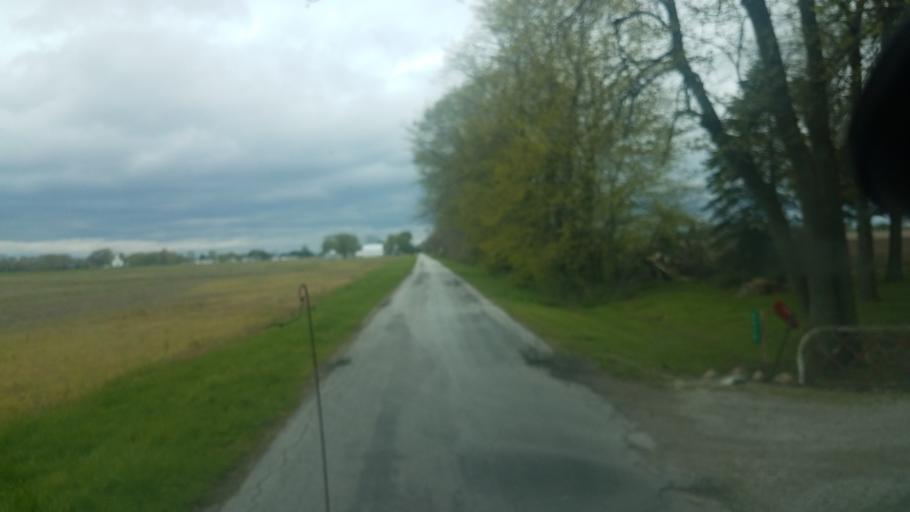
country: US
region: Ohio
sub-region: Marion County
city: Prospect
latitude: 40.5091
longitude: -83.2379
